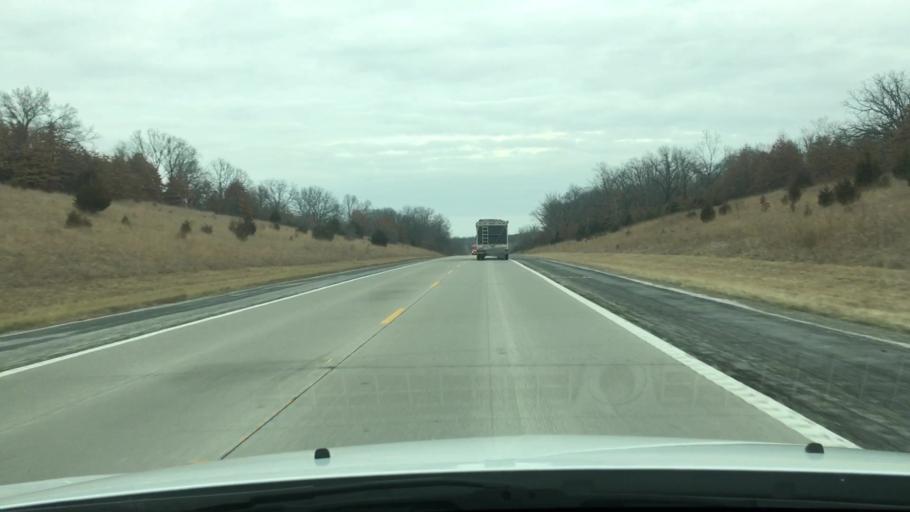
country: US
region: Missouri
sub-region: Audrain County
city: Mexico
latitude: 39.1383
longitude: -91.8511
